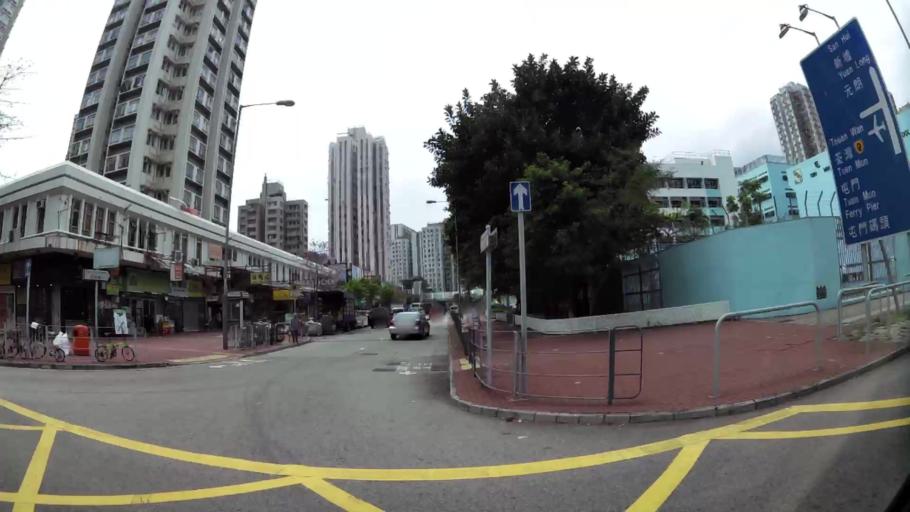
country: HK
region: Tuen Mun
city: Tuen Mun
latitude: 22.3899
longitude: 113.9800
